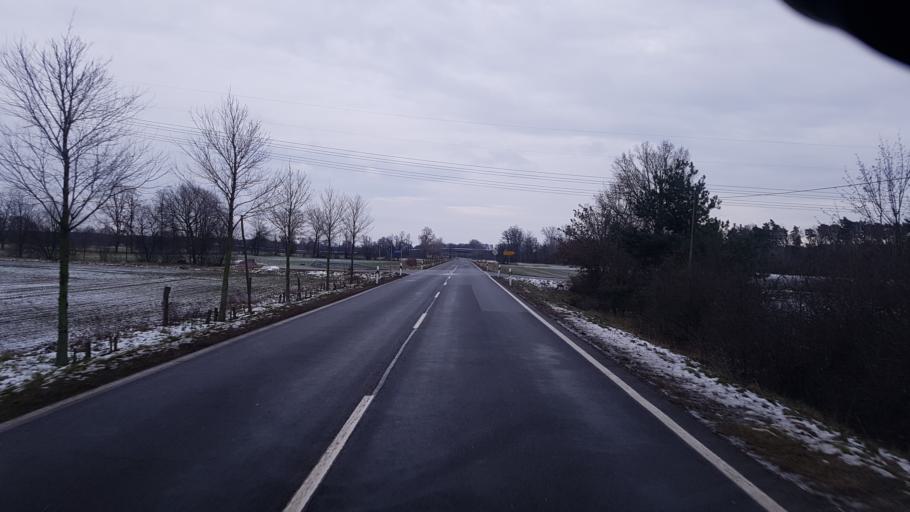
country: DE
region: Brandenburg
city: Heinersbruck
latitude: 51.8297
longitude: 14.4877
